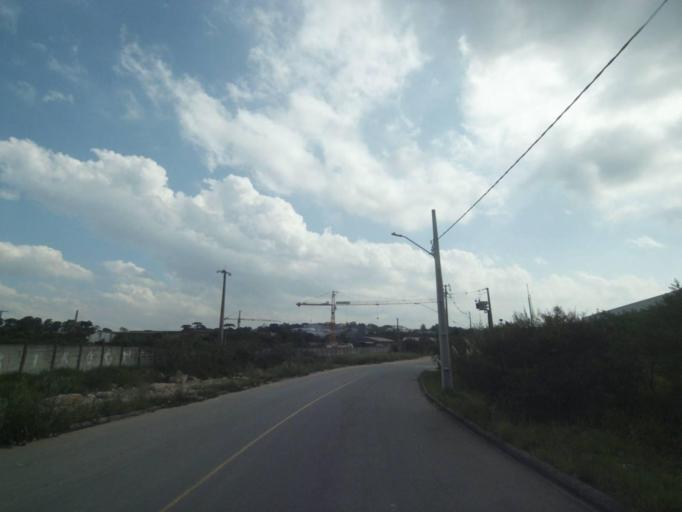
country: BR
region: Parana
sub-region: Curitiba
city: Curitiba
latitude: -25.5113
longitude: -49.3404
